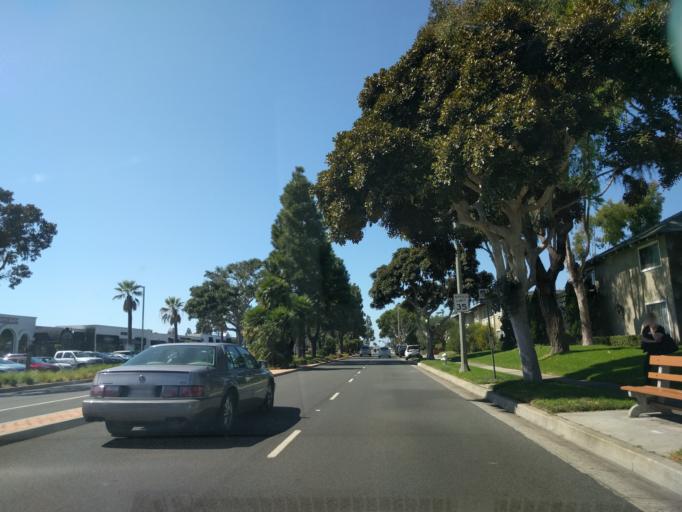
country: US
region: California
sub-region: Orange County
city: Costa Mesa
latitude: 33.6261
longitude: -117.9052
